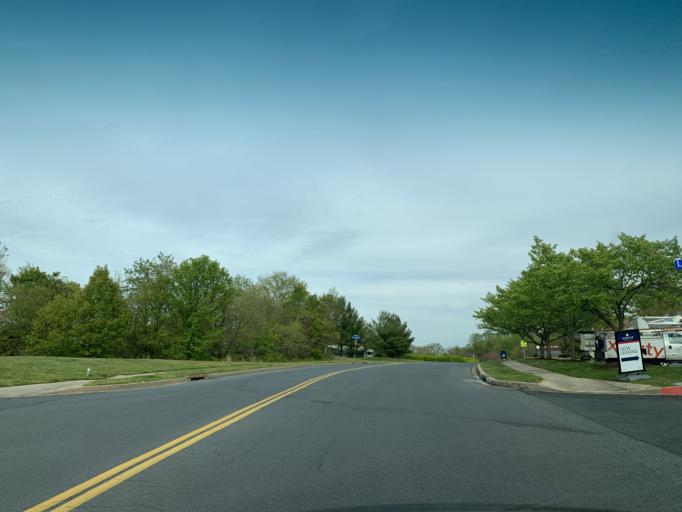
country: US
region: Maryland
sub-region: Harford County
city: Riverside
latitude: 39.4771
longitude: -76.2505
